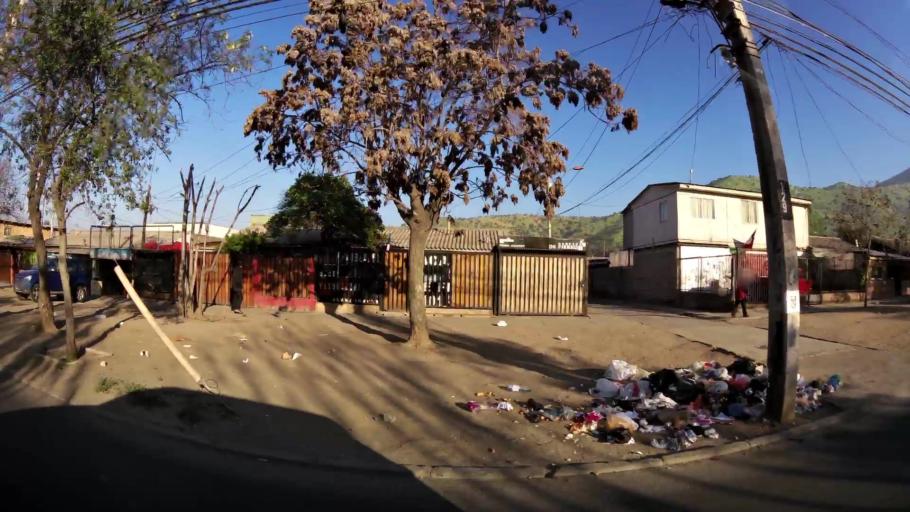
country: CL
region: Santiago Metropolitan
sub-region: Provincia de Santiago
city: Santiago
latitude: -33.3701
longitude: -70.6356
